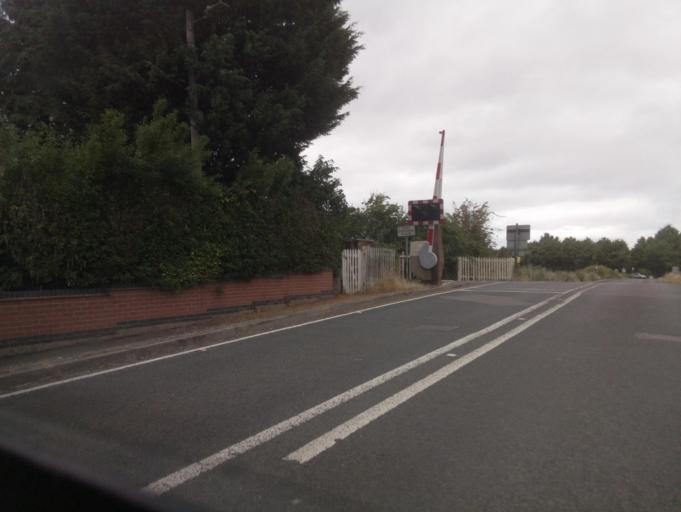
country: GB
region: England
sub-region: Derbyshire
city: Findern
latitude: 52.8574
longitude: -1.5560
